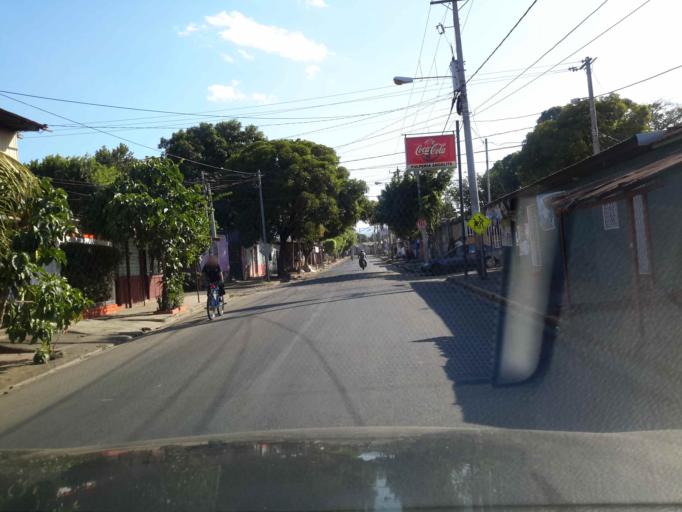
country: NI
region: Managua
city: Managua
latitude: 12.1315
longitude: -86.2528
